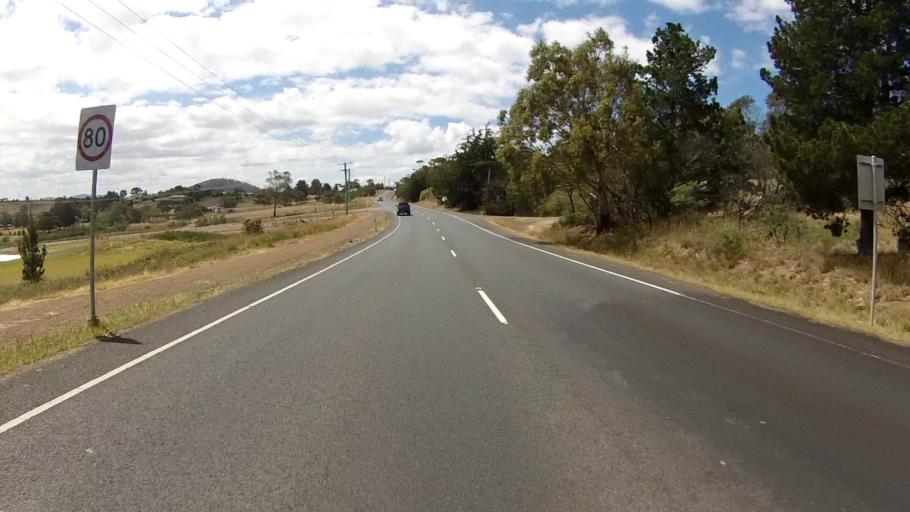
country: AU
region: Tasmania
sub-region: Sorell
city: Sorell
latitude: -42.8226
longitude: 147.6236
